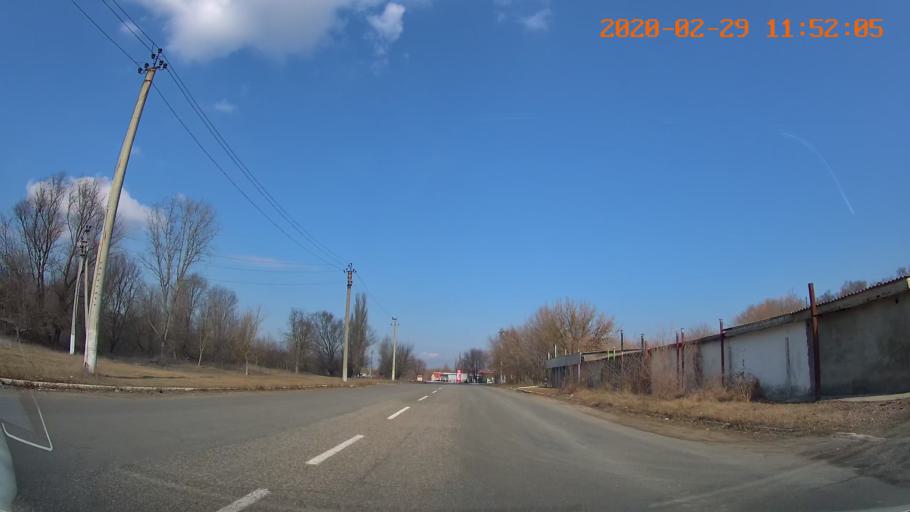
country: MD
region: Telenesti
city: Ribnita
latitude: 47.7696
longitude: 28.9913
